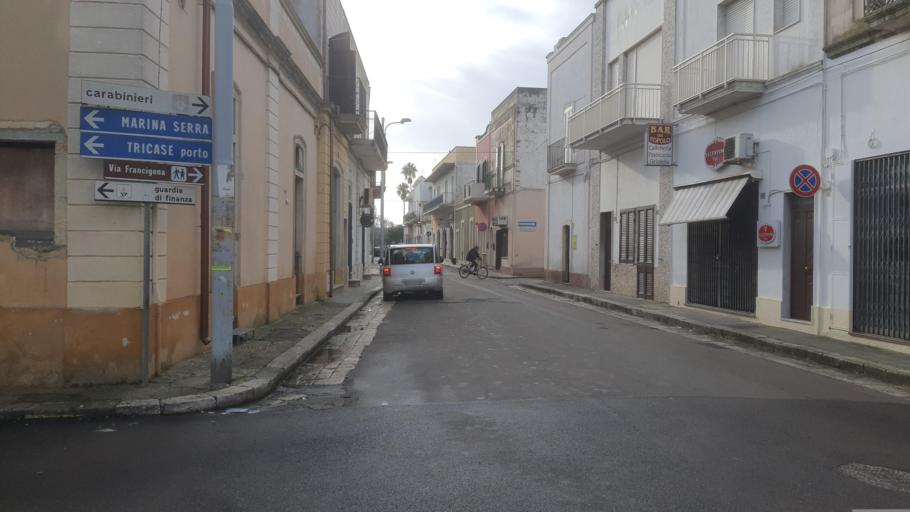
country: IT
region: Apulia
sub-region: Provincia di Lecce
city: Tricase
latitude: 39.9290
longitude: 18.3615
